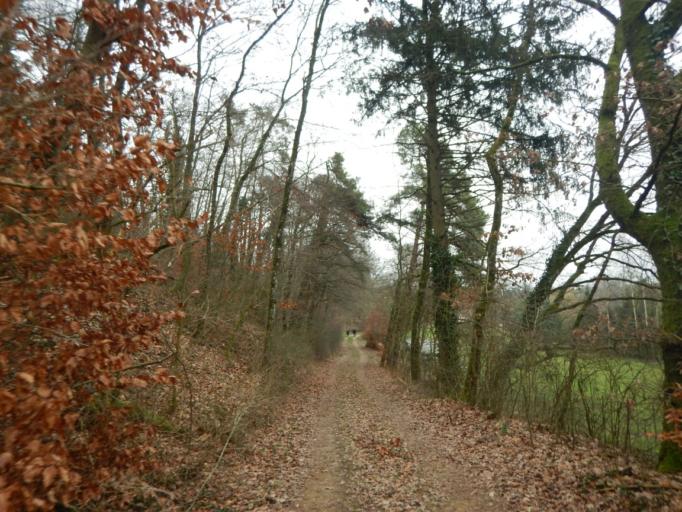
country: LU
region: Luxembourg
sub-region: Canton de Capellen
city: Koerich
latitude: 49.6721
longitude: 5.9402
